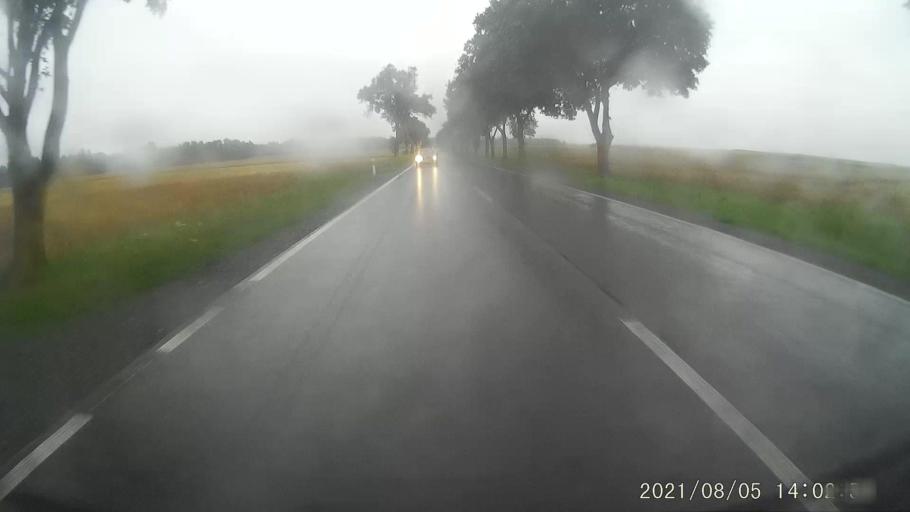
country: PL
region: Opole Voivodeship
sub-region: Powiat krapkowicki
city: Strzeleczki
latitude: 50.4569
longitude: 17.8657
